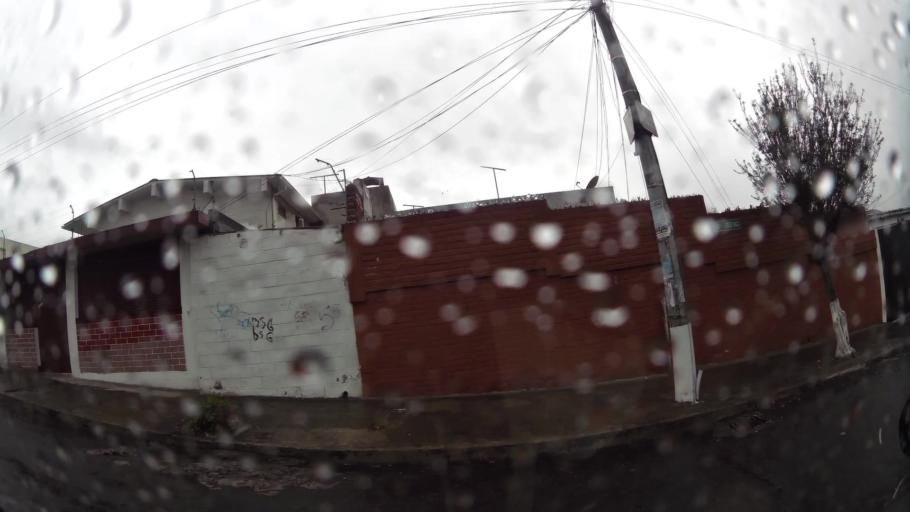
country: EC
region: Pichincha
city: Quito
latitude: -0.1071
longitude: -78.5006
